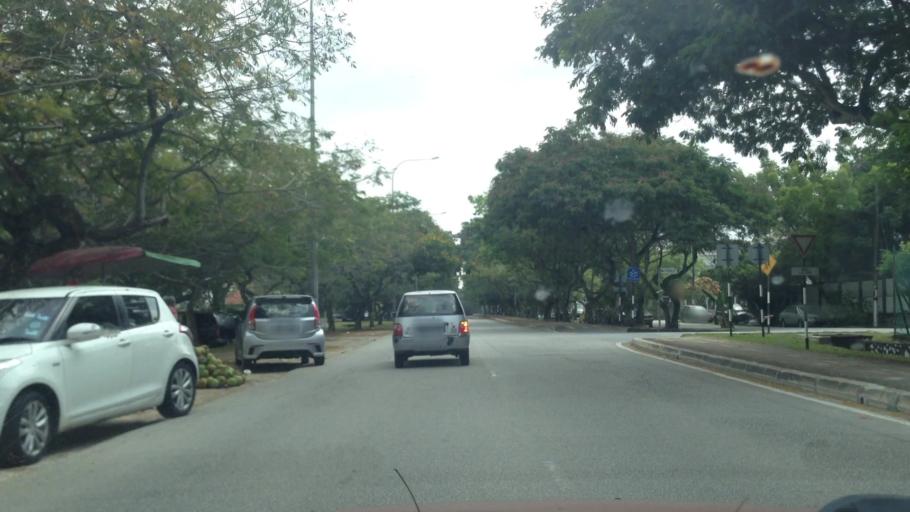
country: MY
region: Selangor
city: Subang Jaya
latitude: 3.0561
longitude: 101.5739
